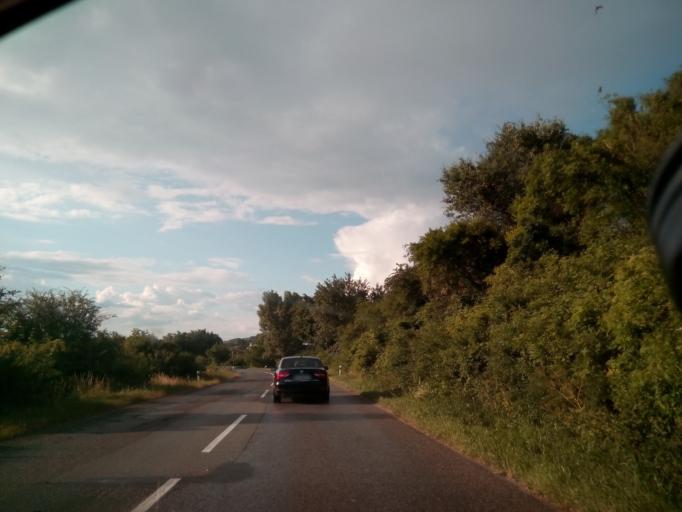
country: SK
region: Kosicky
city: Kosice
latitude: 48.6538
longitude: 21.3600
